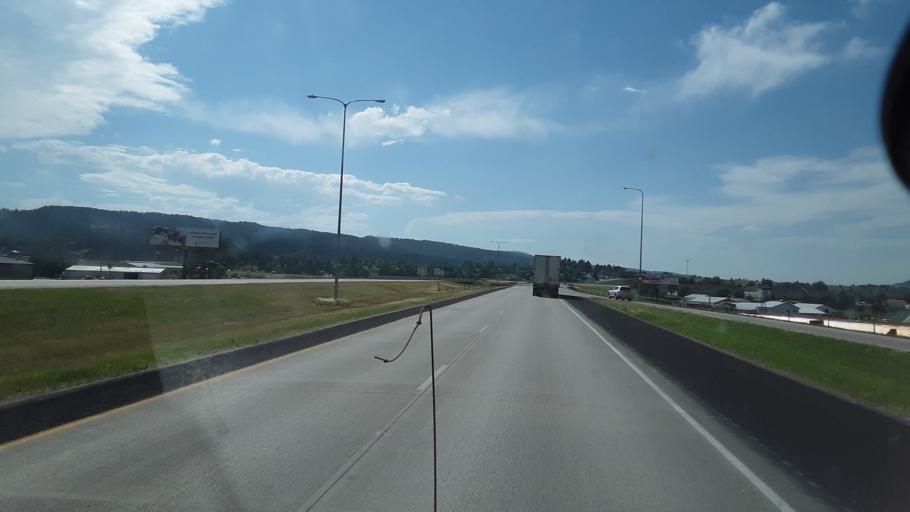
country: US
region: South Dakota
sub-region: Meade County
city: Sturgis
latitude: 44.3961
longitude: -103.5063
